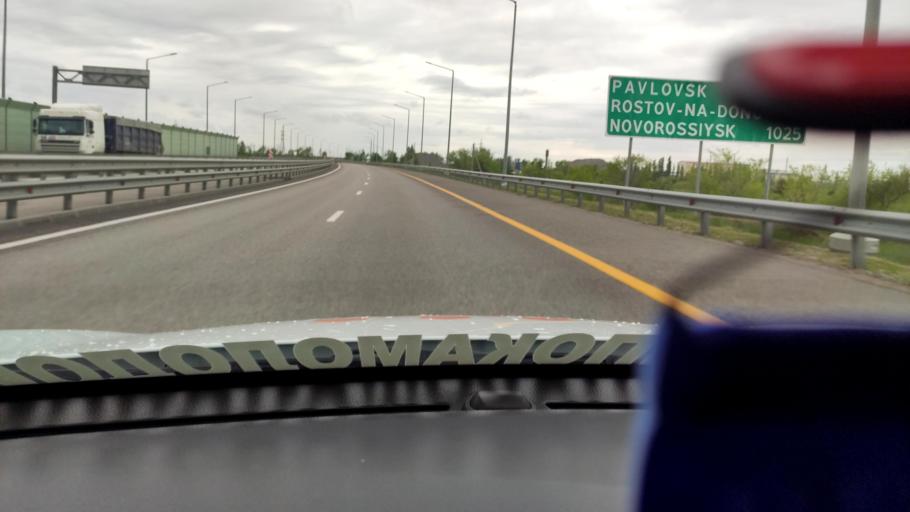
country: RU
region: Voronezj
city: Novaya Usman'
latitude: 51.6346
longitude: 39.3171
